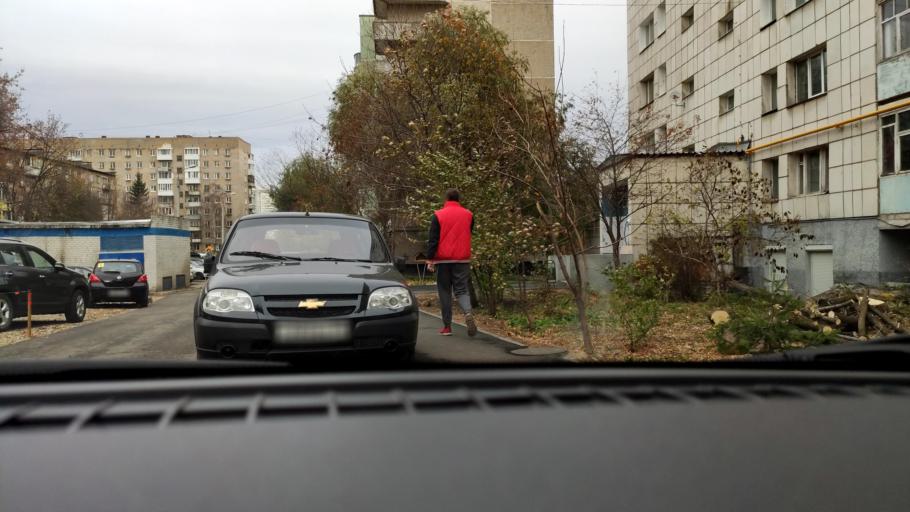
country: RU
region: Perm
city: Perm
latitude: 57.9881
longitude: 56.2747
